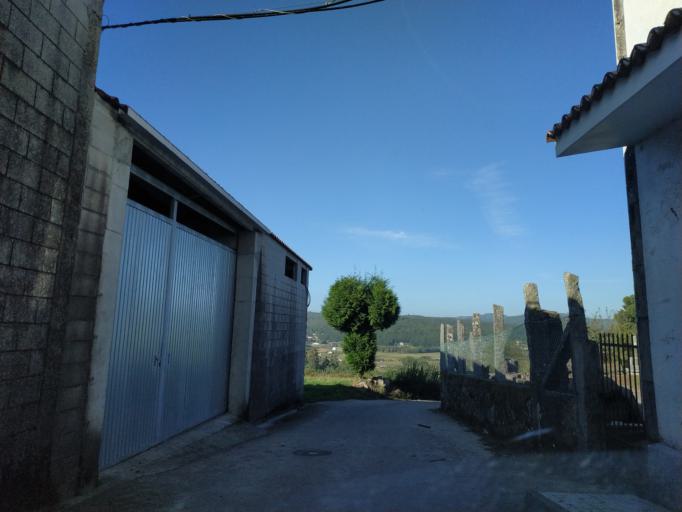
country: ES
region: Galicia
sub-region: Provincia da Coruna
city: Negreira
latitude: 42.9128
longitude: -8.7647
